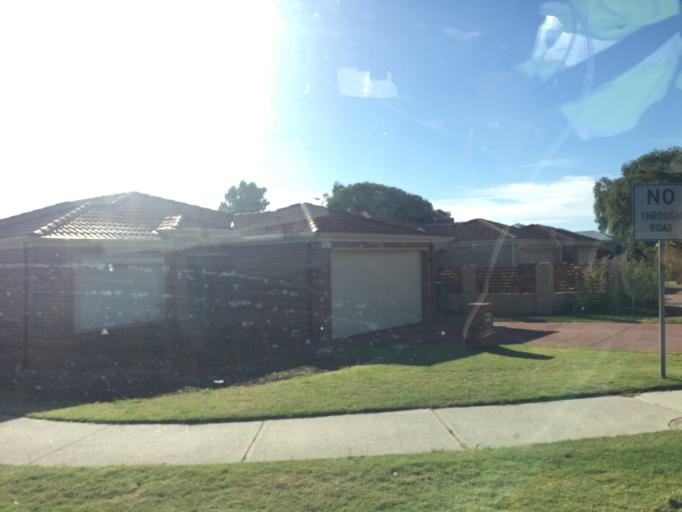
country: AU
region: Western Australia
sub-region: Belmont
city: Rivervale
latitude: -31.9648
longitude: 115.9239
